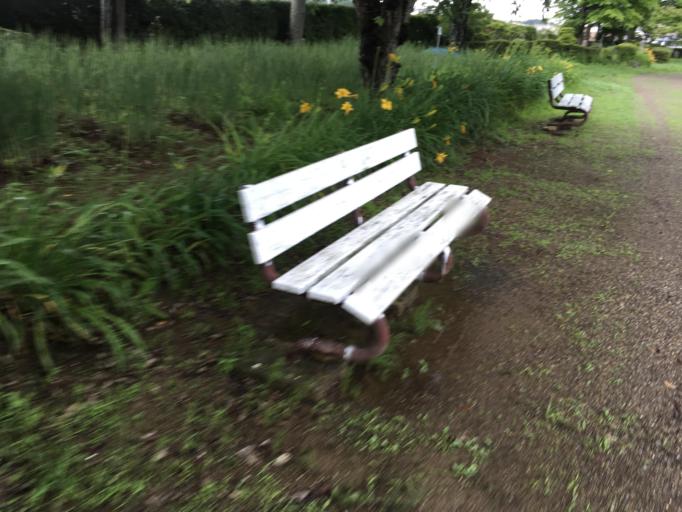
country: JP
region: Miyagi
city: Furukawa
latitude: 38.7426
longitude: 140.9491
